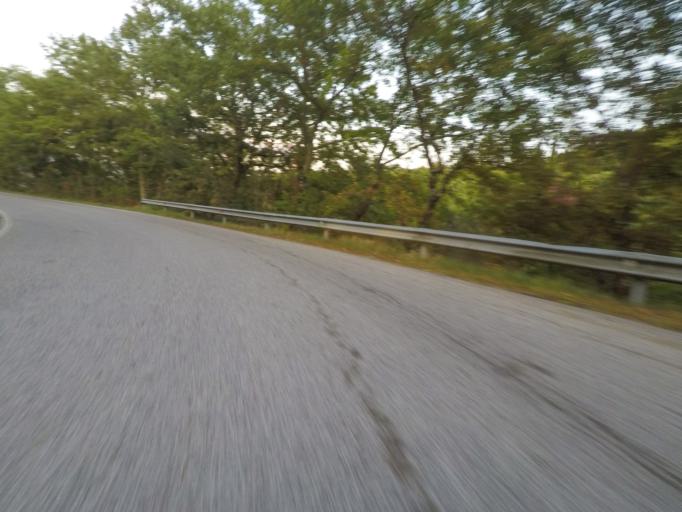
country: IT
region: Tuscany
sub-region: Provincia di Siena
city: Torrita di Siena
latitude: 43.1456
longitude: 11.7398
